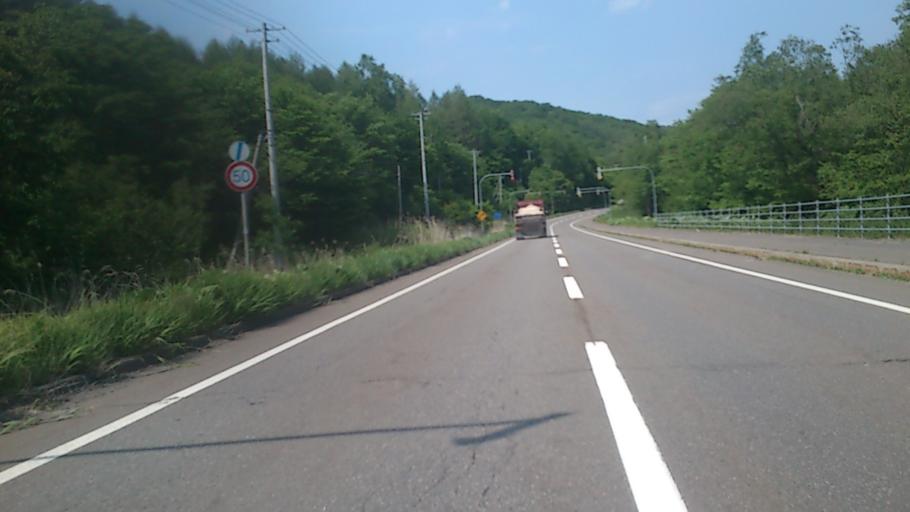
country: JP
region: Hokkaido
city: Otofuke
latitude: 43.2521
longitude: 143.5653
